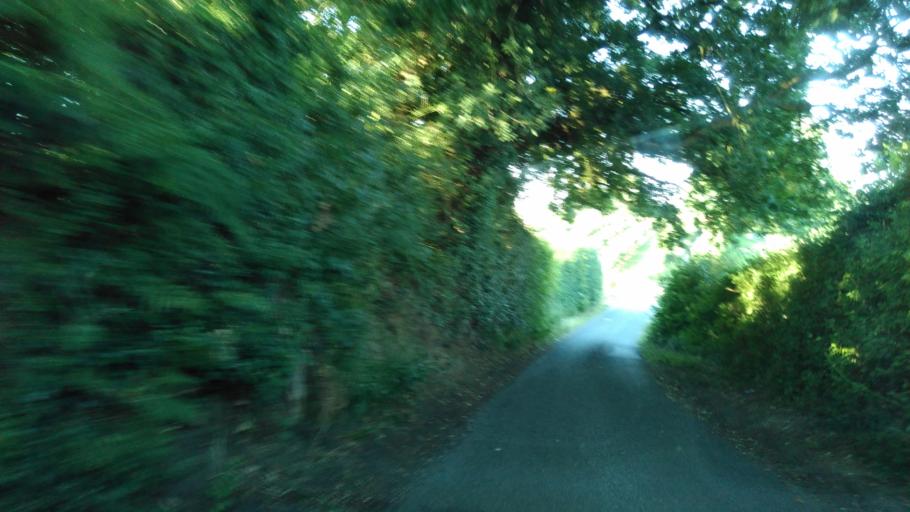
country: GB
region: England
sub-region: Kent
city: Chartham
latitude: 51.2678
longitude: 1.0134
